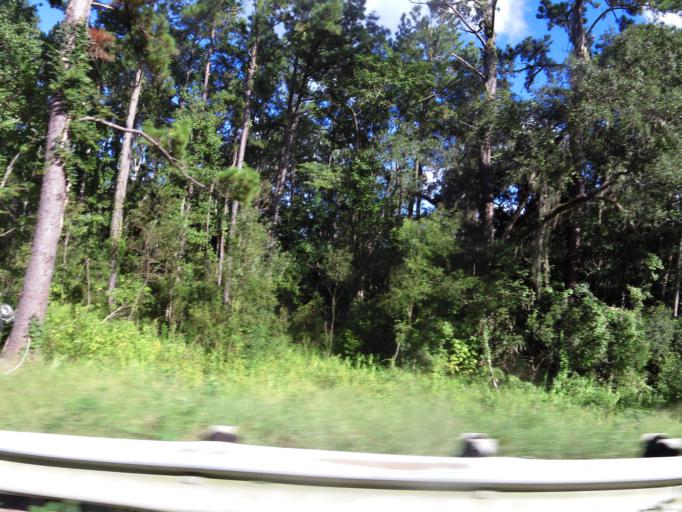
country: US
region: Georgia
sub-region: Glynn County
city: Dock Junction
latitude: 31.1335
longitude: -81.5984
